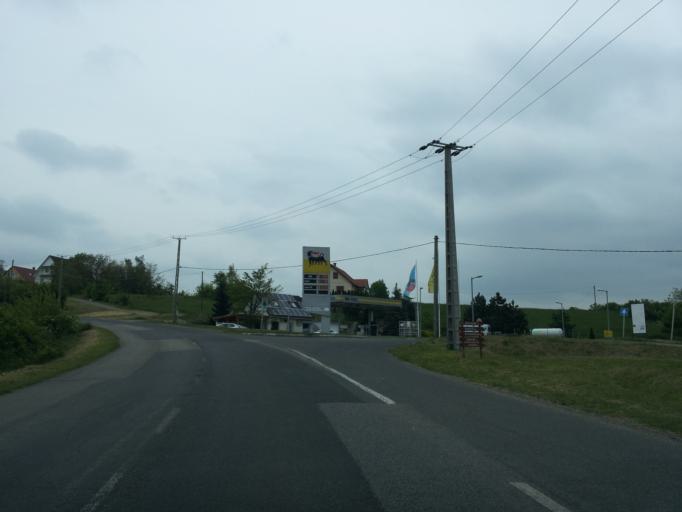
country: HU
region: Baranya
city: Hosszuheteny
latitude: 46.1468
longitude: 18.3520
